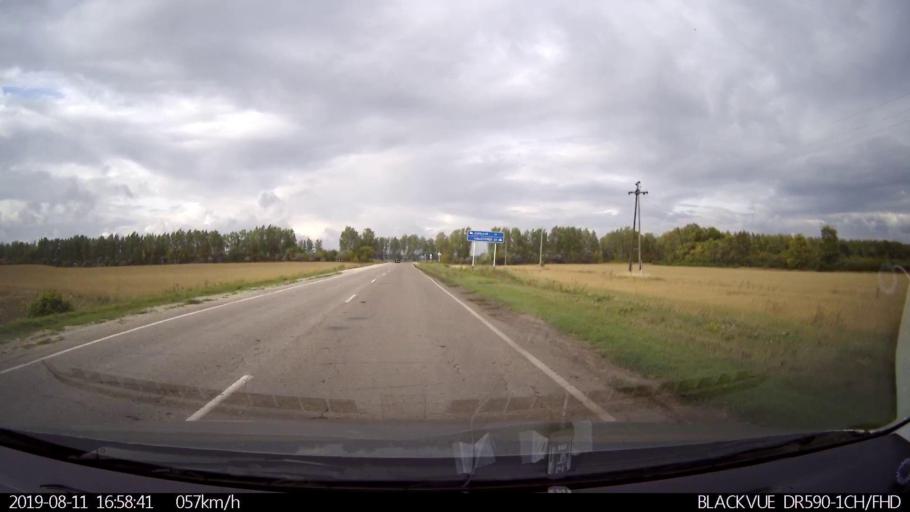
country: RU
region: Ulyanovsk
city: Mayna
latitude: 54.3104
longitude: 47.6568
